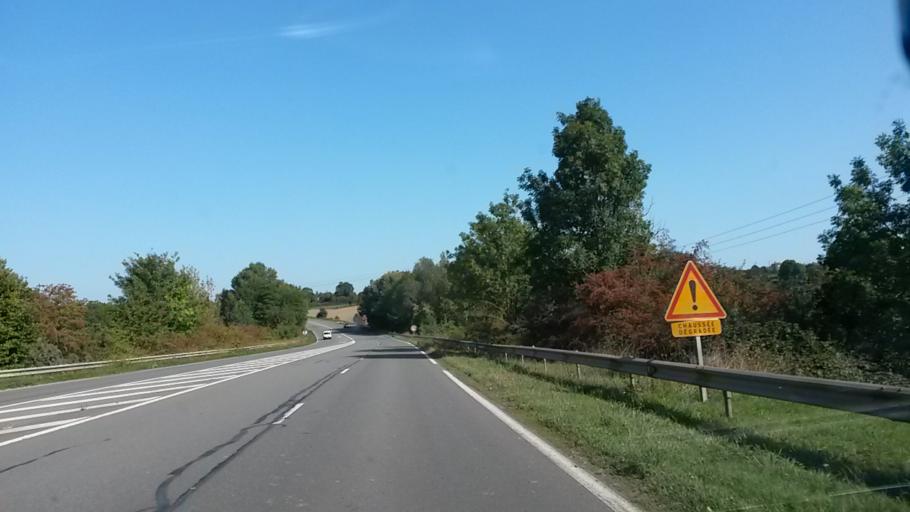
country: FR
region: Nord-Pas-de-Calais
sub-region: Departement du Nord
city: Avesnes-sur-Helpe
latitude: 50.0588
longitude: 3.9331
